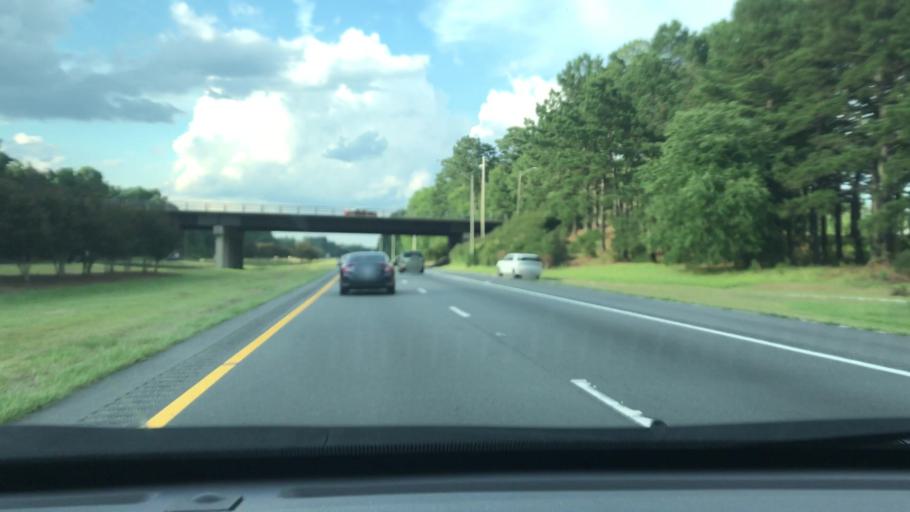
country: US
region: North Carolina
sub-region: Cumberland County
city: Vander
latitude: 35.0063
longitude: -78.8209
